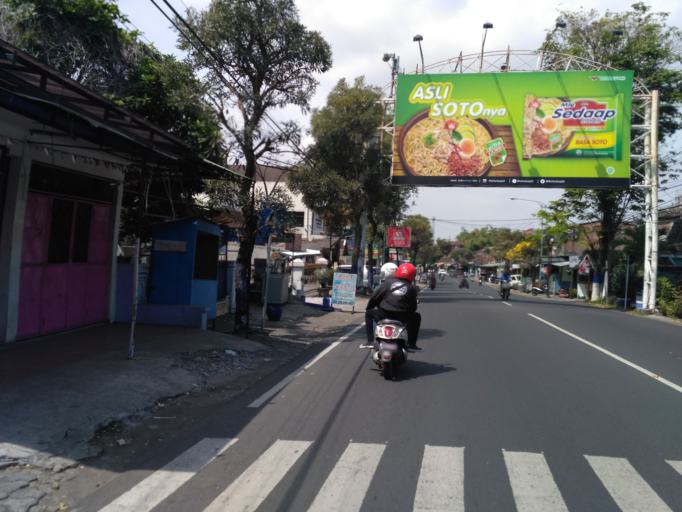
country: ID
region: East Java
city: Malang
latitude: -7.9169
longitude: 112.5883
